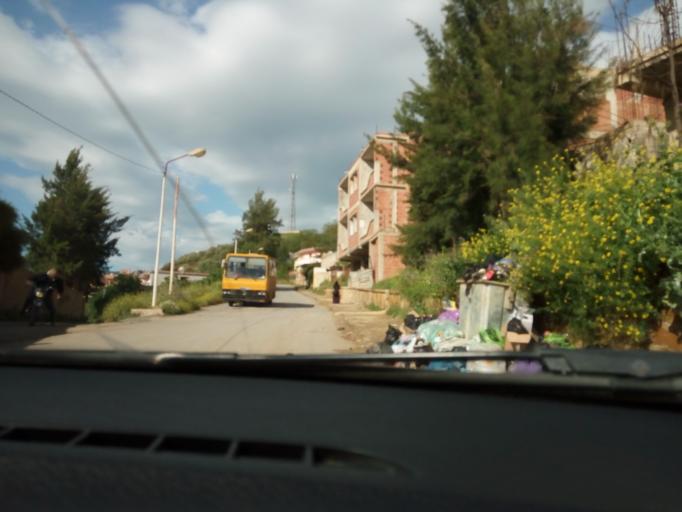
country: DZ
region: Tipaza
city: Hadjout
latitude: 36.3718
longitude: 2.4793
